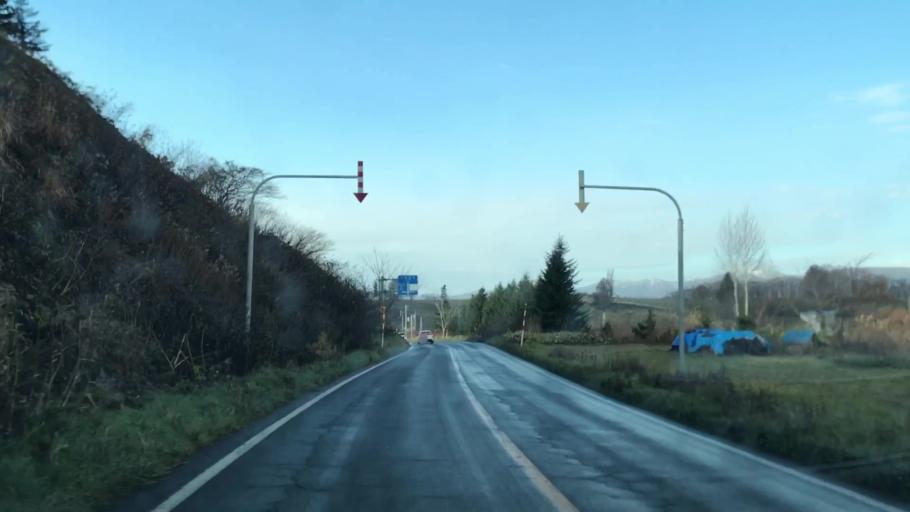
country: JP
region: Hokkaido
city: Yoichi
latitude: 43.1795
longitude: 140.8243
